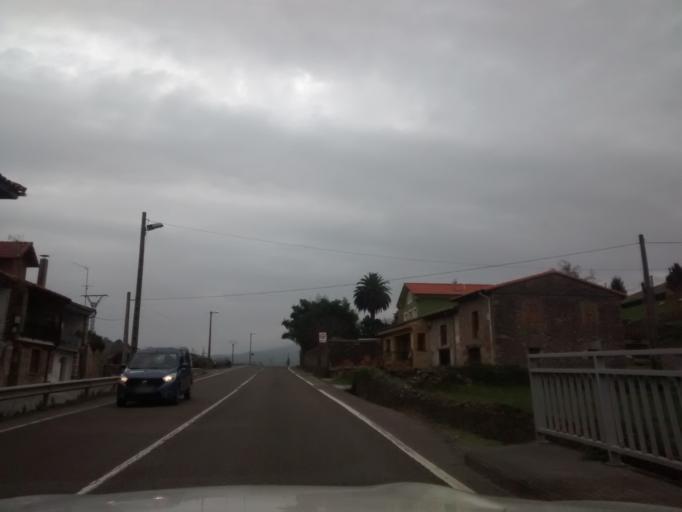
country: ES
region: Cantabria
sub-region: Provincia de Cantabria
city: Corvera
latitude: 43.2839
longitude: -3.9522
